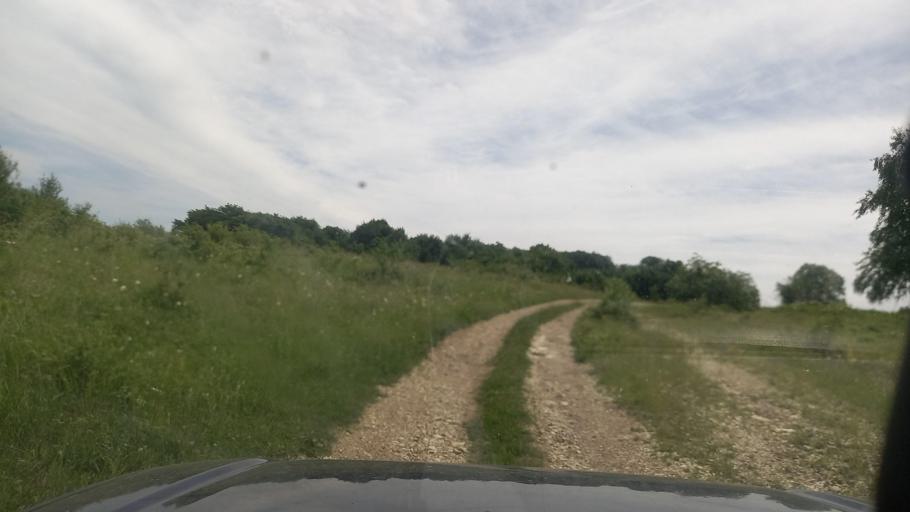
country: RU
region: Karachayevo-Cherkesiya
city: Pregradnaya
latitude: 44.0975
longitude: 41.1287
